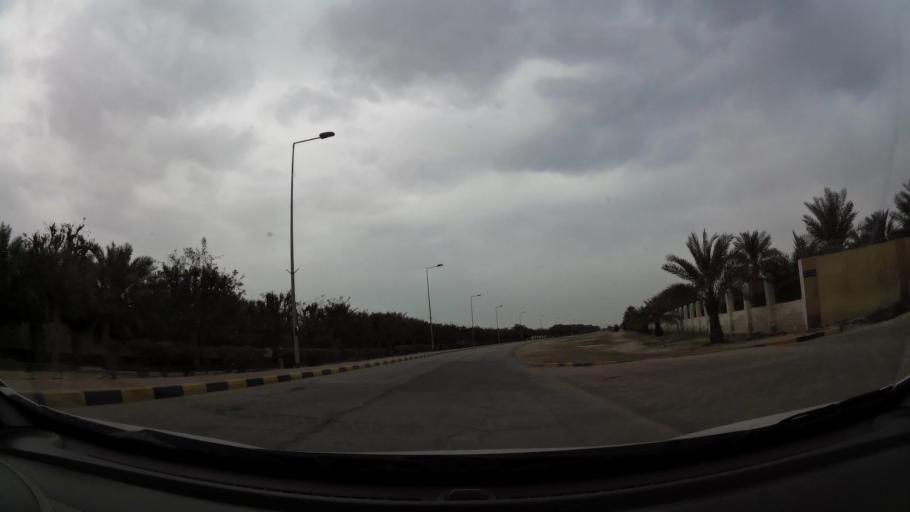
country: BH
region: Central Governorate
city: Dar Kulayb
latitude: 26.0415
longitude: 50.4885
